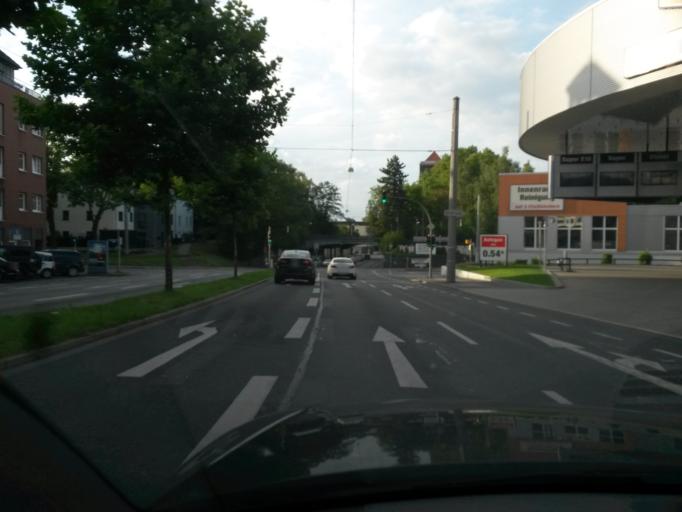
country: DE
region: North Rhine-Westphalia
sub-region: Regierungsbezirk Arnsberg
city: Dortmund
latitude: 51.5073
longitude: 7.4749
